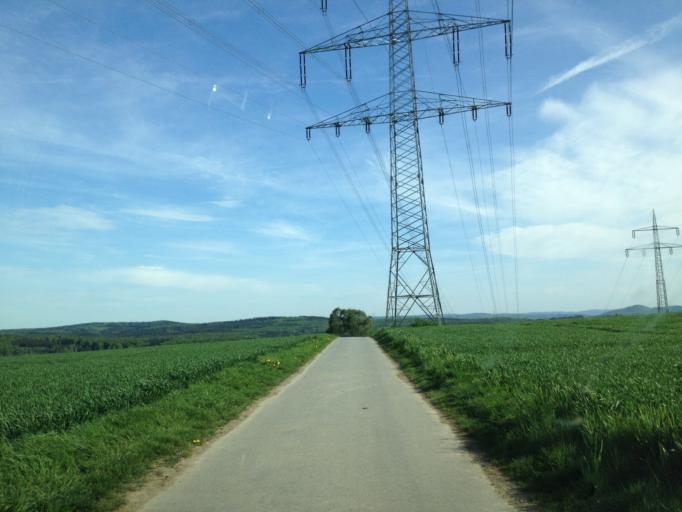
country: DE
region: North Rhine-Westphalia
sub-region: Regierungsbezirk Arnsberg
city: Werl
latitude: 51.4835
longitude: 7.9809
